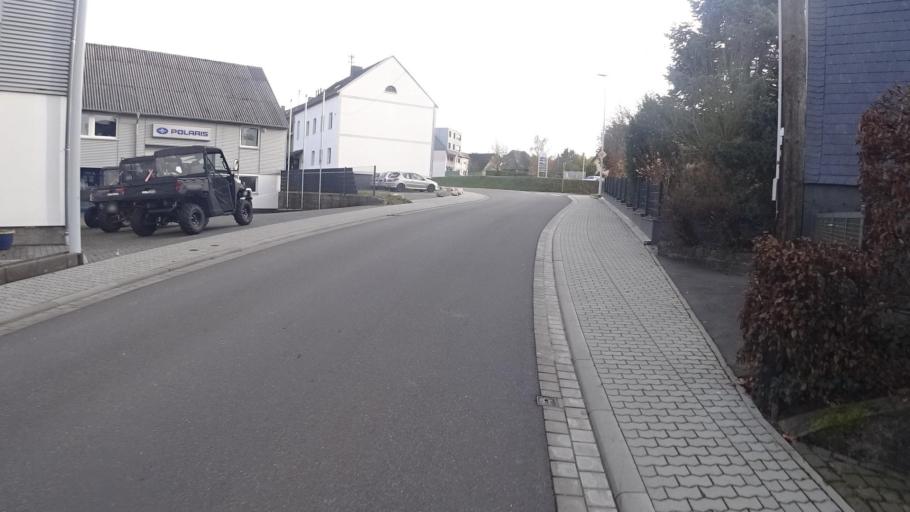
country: DE
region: Rheinland-Pfalz
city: Pfalzfeld
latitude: 50.1145
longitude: 7.5774
